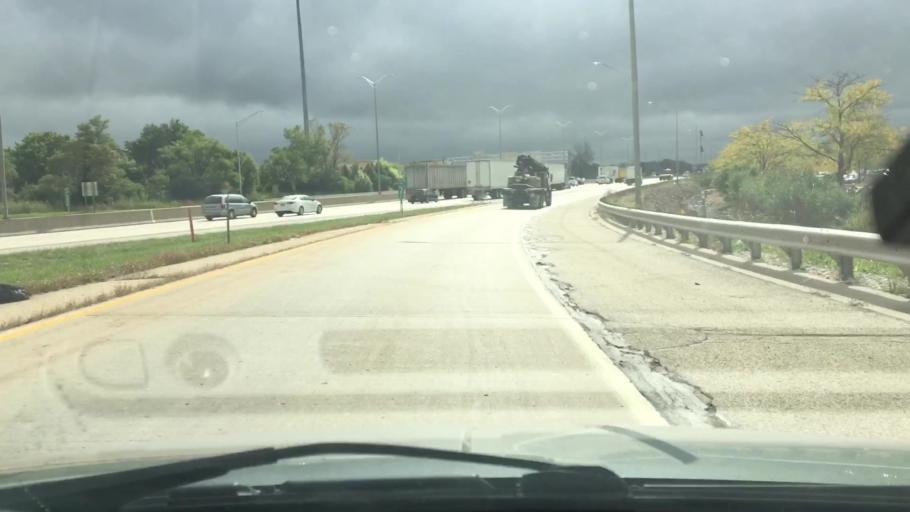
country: US
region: Illinois
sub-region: Lake County
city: Lincolnshire
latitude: 42.1983
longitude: -87.8881
